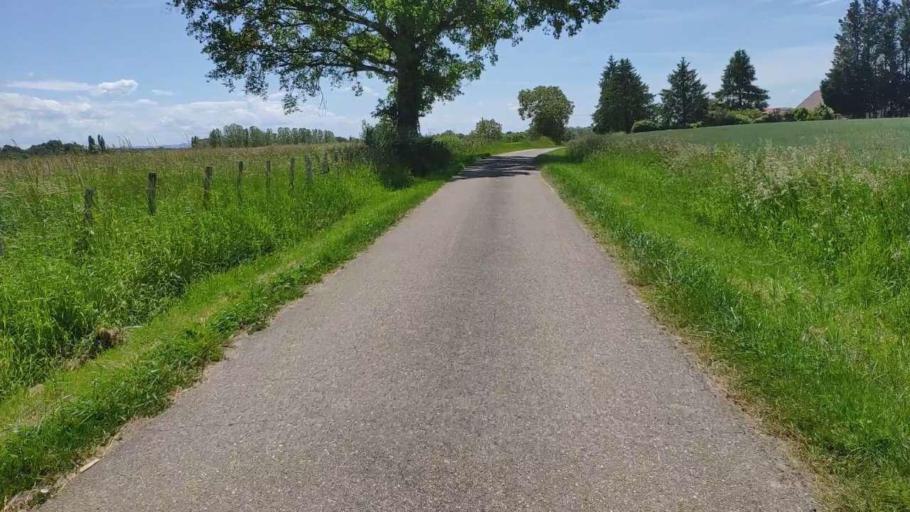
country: FR
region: Franche-Comte
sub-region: Departement du Jura
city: Bletterans
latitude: 46.7943
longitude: 5.3914
